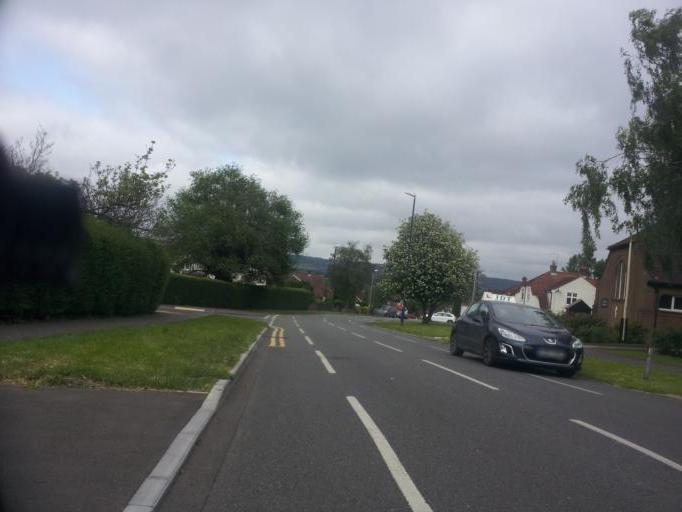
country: GB
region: England
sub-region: Kent
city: Maidstone
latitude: 51.2816
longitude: 0.4994
